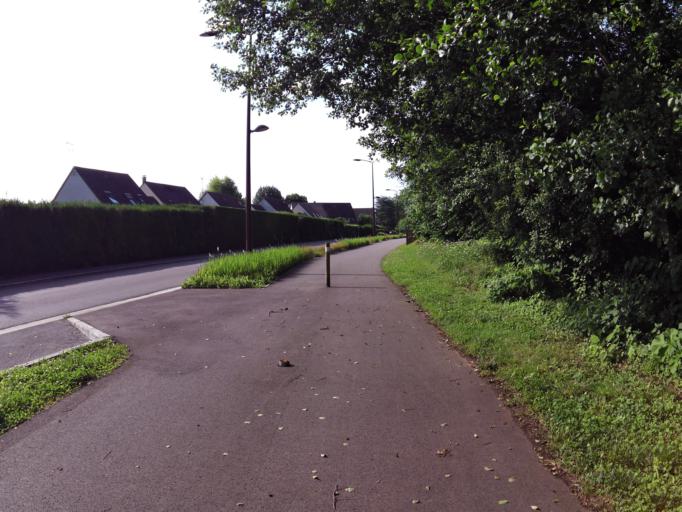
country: FR
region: Champagne-Ardenne
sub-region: Departement de l'Aube
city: Saint-Julien-les-Villas
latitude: 48.2764
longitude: 4.0999
